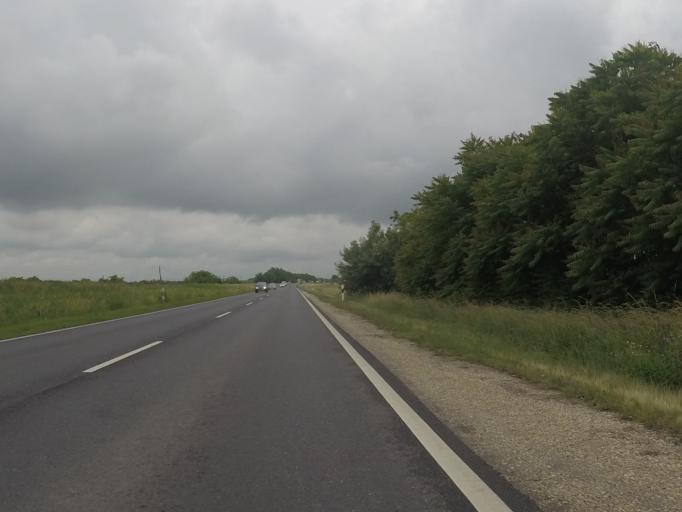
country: HU
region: Gyor-Moson-Sopron
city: Gyorujbarat
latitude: 47.6263
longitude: 17.6745
